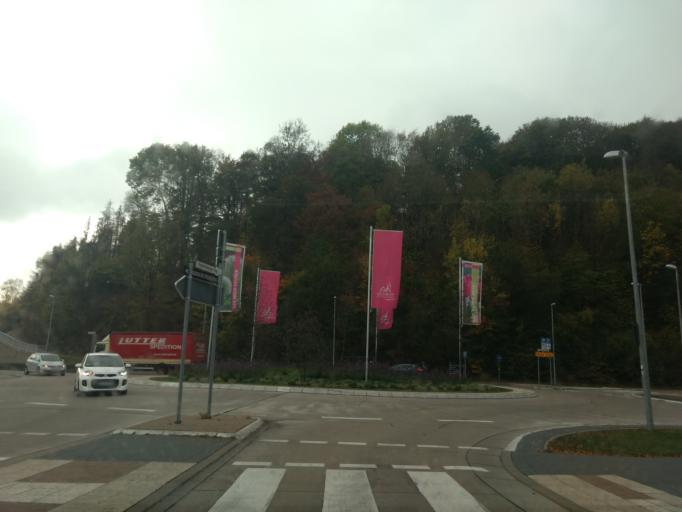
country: DE
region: Lower Saxony
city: Bad Iburg
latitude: 52.1595
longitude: 8.0383
